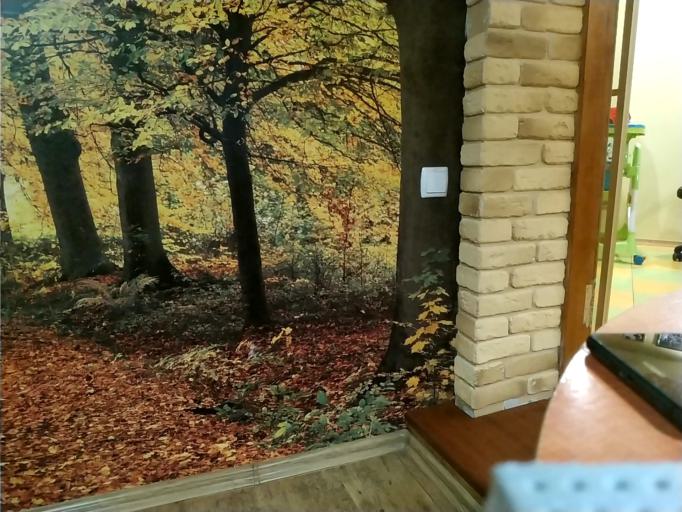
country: RU
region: Tverskaya
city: Zubtsov
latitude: 56.2584
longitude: 34.6981
